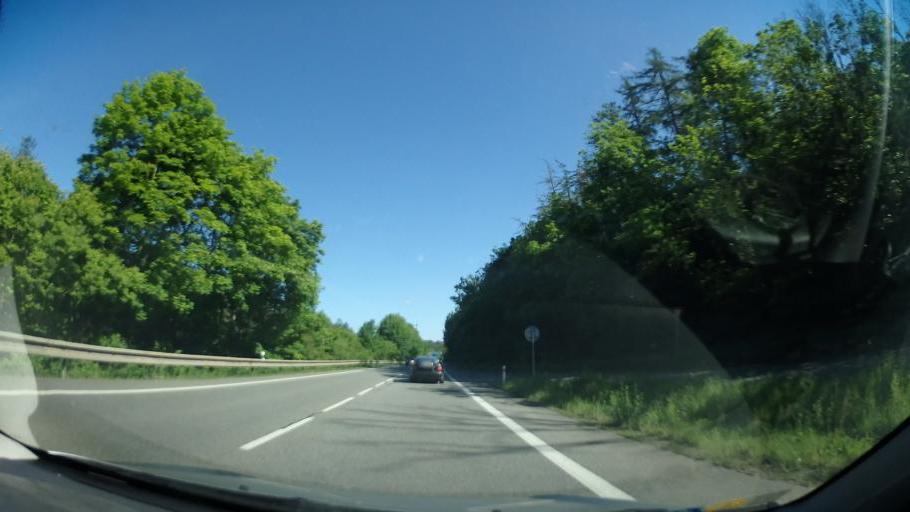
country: CZ
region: South Moravian
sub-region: Okres Blansko
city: Letovice
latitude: 49.5290
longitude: 16.5818
